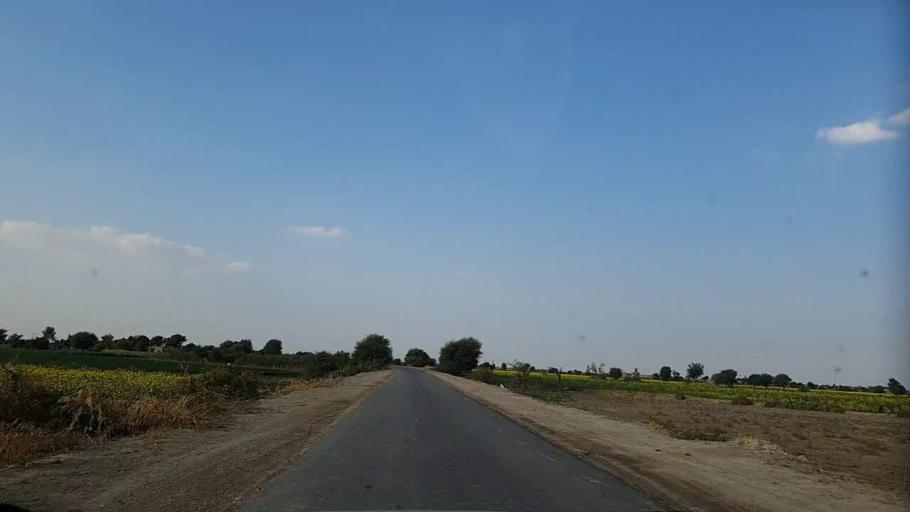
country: PK
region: Sindh
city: Pithoro
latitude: 25.6829
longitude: 69.2258
